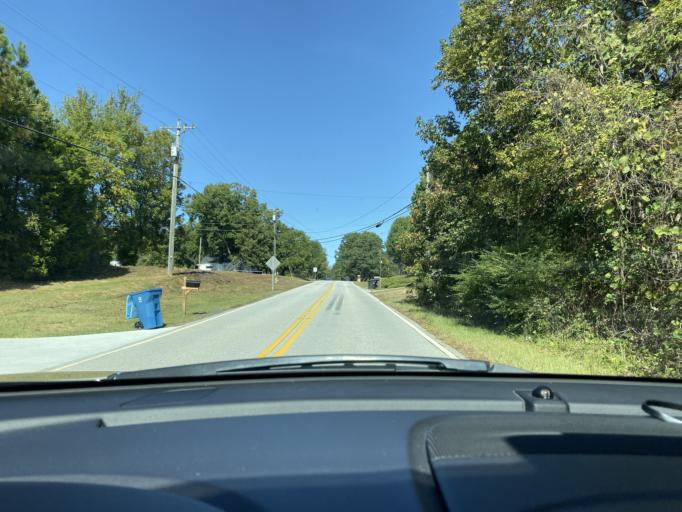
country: US
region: Georgia
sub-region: Gwinnett County
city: Grayson
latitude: 33.8908
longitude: -83.9051
